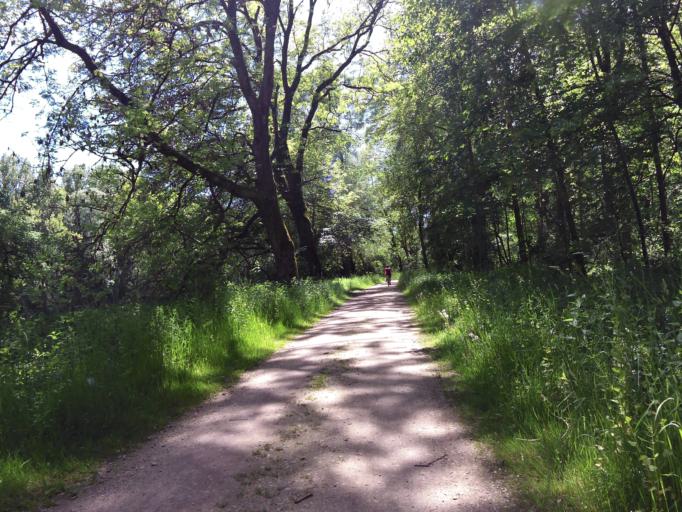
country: DE
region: Bavaria
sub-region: Upper Bavaria
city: Freising
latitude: 48.3895
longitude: 11.7459
